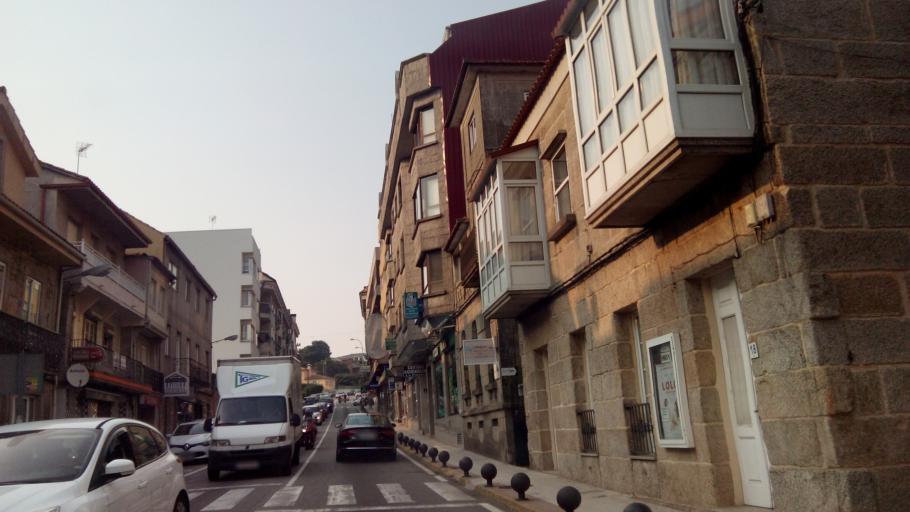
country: ES
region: Galicia
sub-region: Provincia de Pontevedra
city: Nigran
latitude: 42.1165
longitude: -8.8126
